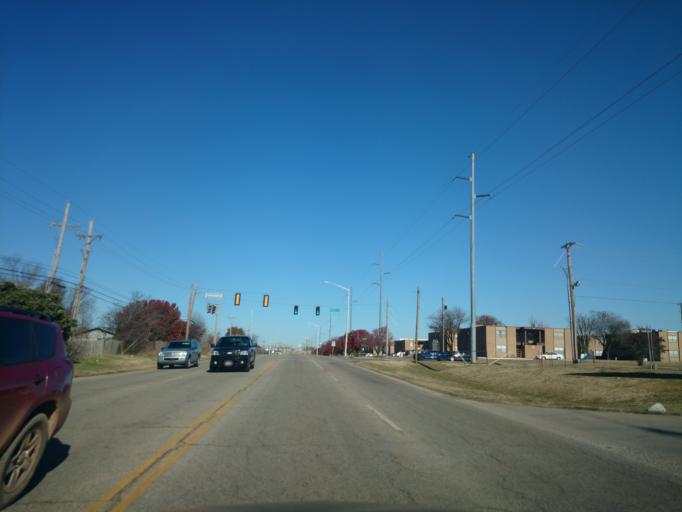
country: US
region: Oklahoma
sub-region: Payne County
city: Stillwater
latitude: 36.1479
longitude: -97.0516
